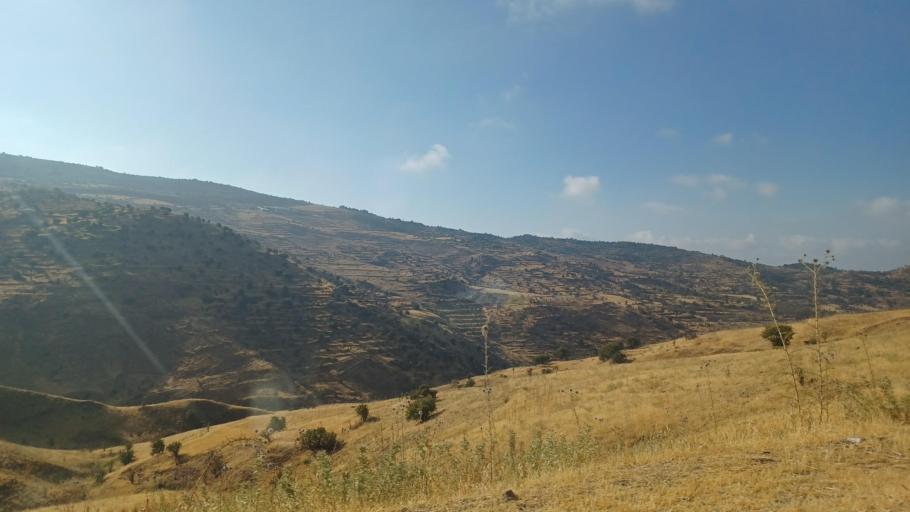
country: CY
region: Pafos
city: Mesogi
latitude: 34.8642
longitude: 32.6012
